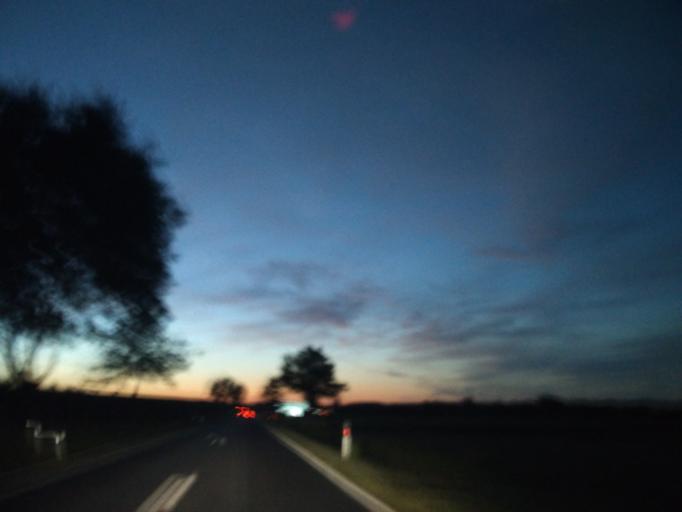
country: HU
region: Vas
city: Vasvar
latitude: 46.9658
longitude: 16.8432
